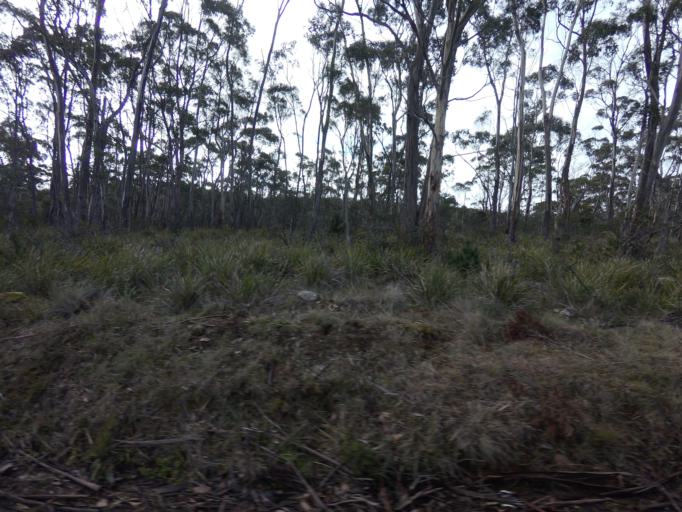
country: AU
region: Tasmania
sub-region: Derwent Valley
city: New Norfolk
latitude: -42.7567
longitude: 146.8831
